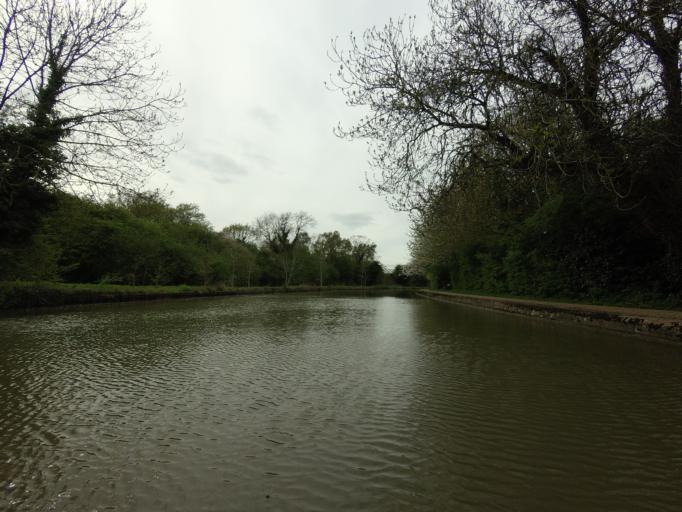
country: GB
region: England
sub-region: Milton Keynes
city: Bradwell
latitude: 52.0602
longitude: -0.8008
